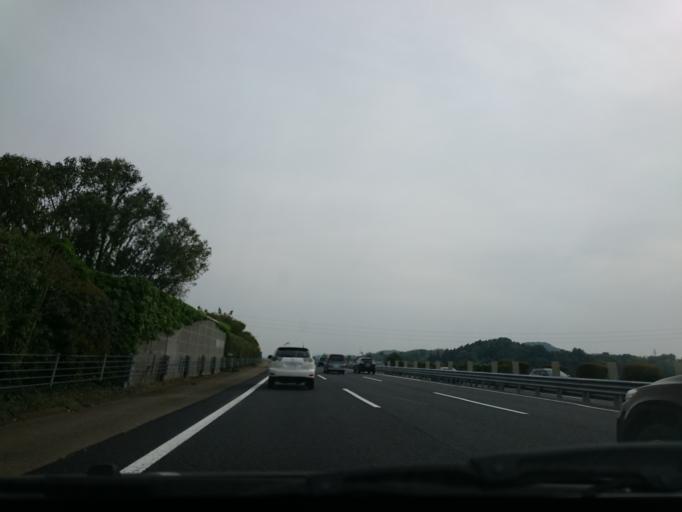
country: JP
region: Tochigi
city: Kanuma
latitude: 36.4881
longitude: 139.7366
